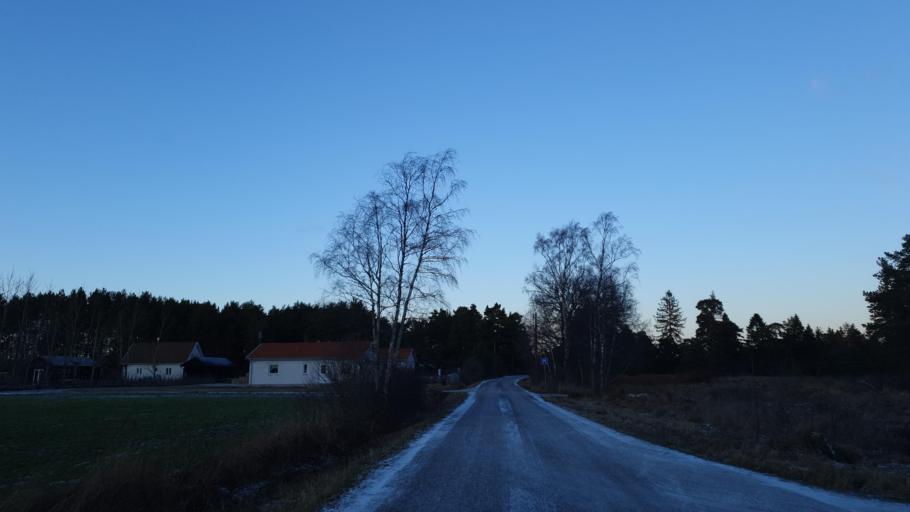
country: SE
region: Gotland
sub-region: Gotland
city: Slite
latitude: 57.3846
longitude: 18.8086
